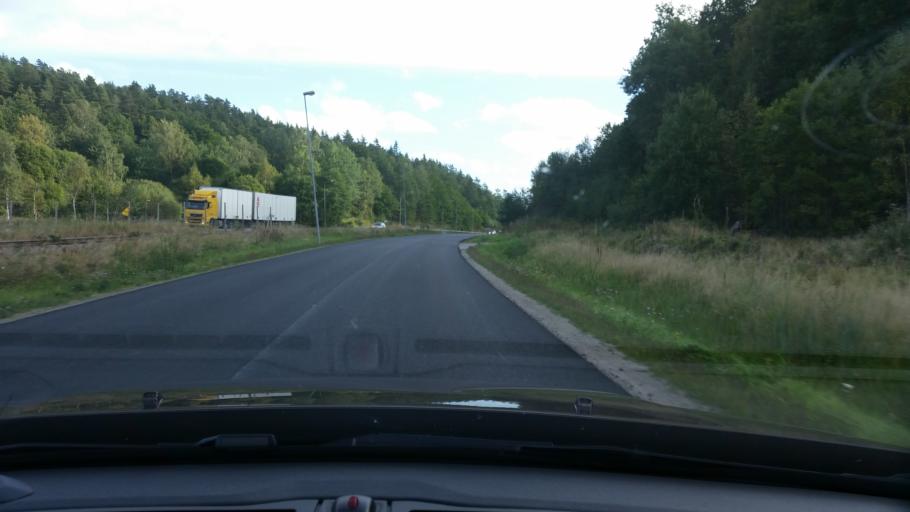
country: SE
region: Vaestra Goetaland
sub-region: Lilla Edets Kommun
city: Lilla Edet
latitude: 58.1152
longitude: 12.1414
